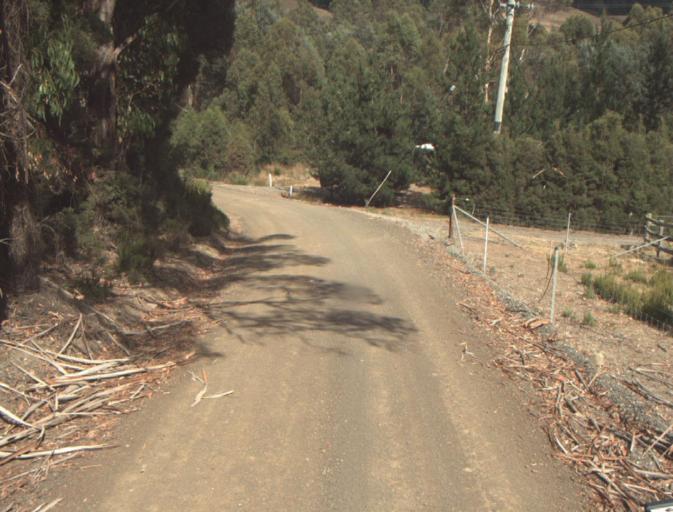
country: AU
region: Tasmania
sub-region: Launceston
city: Mayfield
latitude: -41.2737
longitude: 147.2232
